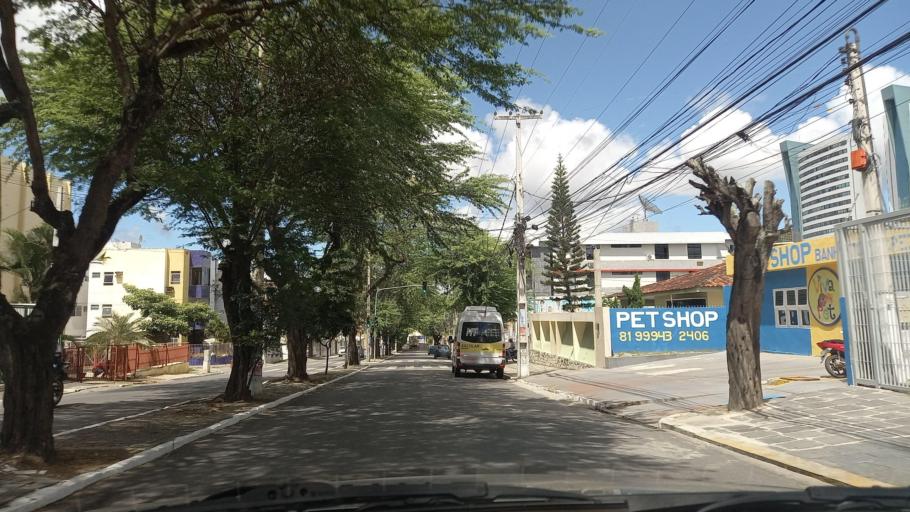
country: BR
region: Pernambuco
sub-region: Caruaru
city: Caruaru
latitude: -8.2705
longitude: -35.9641
